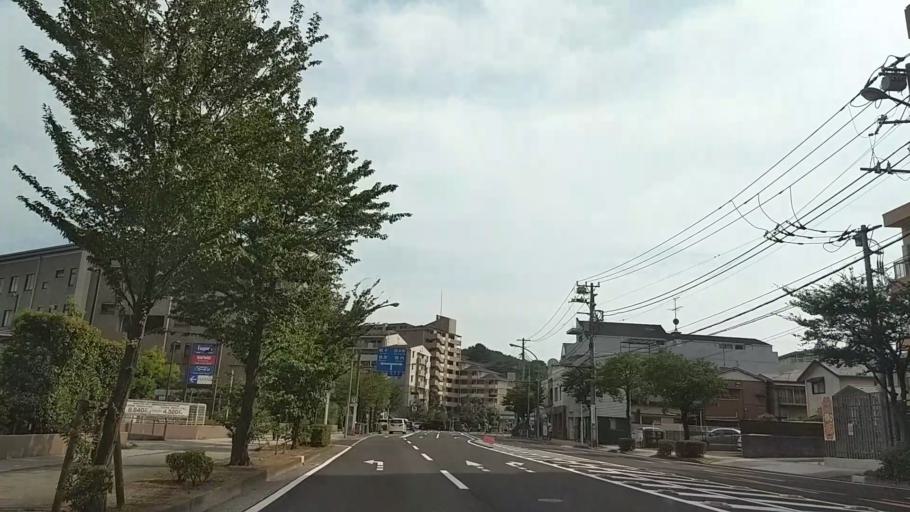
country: JP
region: Kanagawa
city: Yokohama
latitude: 35.4304
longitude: 139.6642
